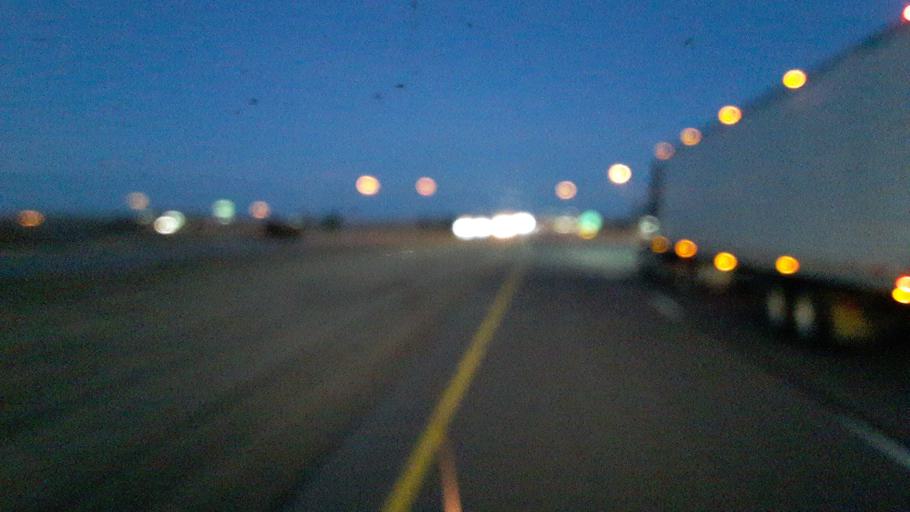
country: US
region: Nebraska
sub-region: Lincoln County
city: Sutherland
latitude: 41.1102
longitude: -101.3620
